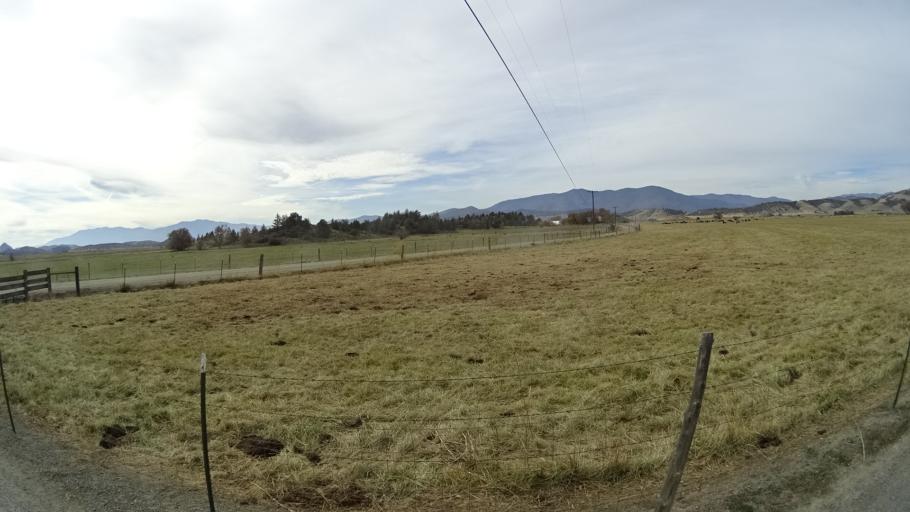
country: US
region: California
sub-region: Siskiyou County
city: Montague
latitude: 41.6624
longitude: -122.5018
